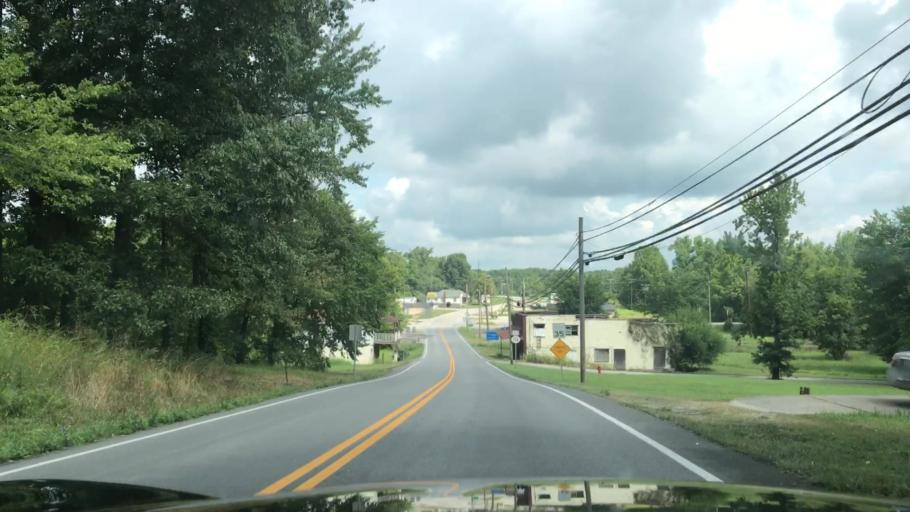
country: US
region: Kentucky
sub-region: Muhlenberg County
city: Central City
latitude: 37.2171
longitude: -87.0452
